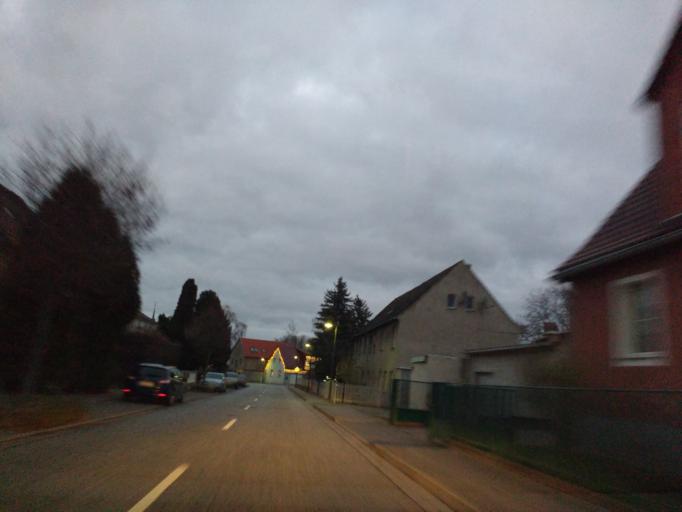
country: DE
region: Saxony-Anhalt
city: Bad Lauchstadt
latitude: 51.3841
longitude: 11.8639
